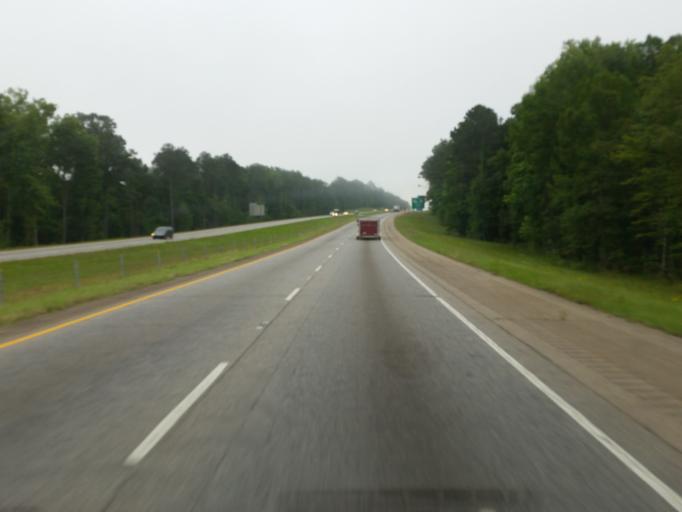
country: US
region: Louisiana
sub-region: Webster Parish
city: Minden
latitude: 32.5938
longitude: -93.3112
